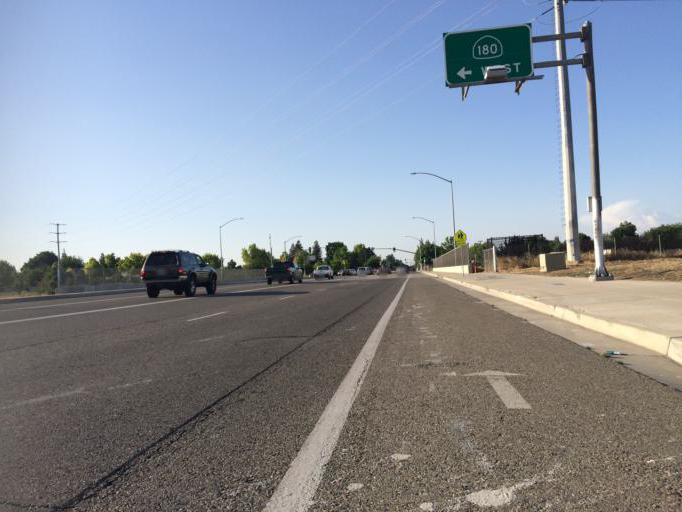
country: US
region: California
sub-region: Fresno County
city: Sunnyside
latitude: 36.7525
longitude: -119.7181
